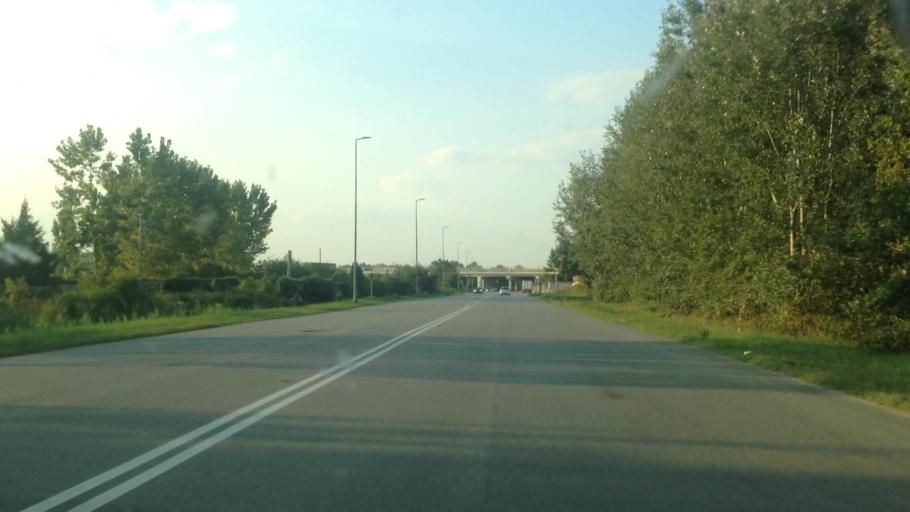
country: IT
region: Piedmont
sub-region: Provincia di Asti
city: Asti
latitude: 44.9094
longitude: 8.2305
